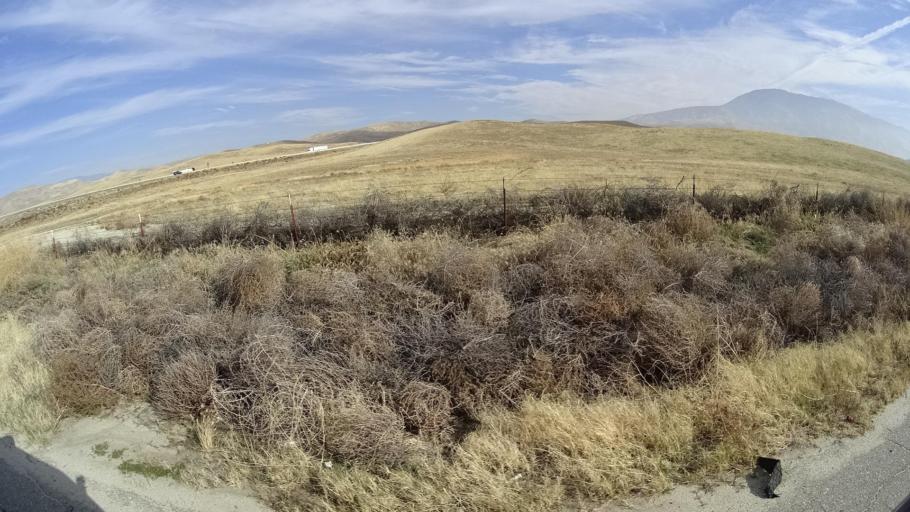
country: US
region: California
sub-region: Kern County
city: Arvin
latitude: 35.2902
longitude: -118.7527
